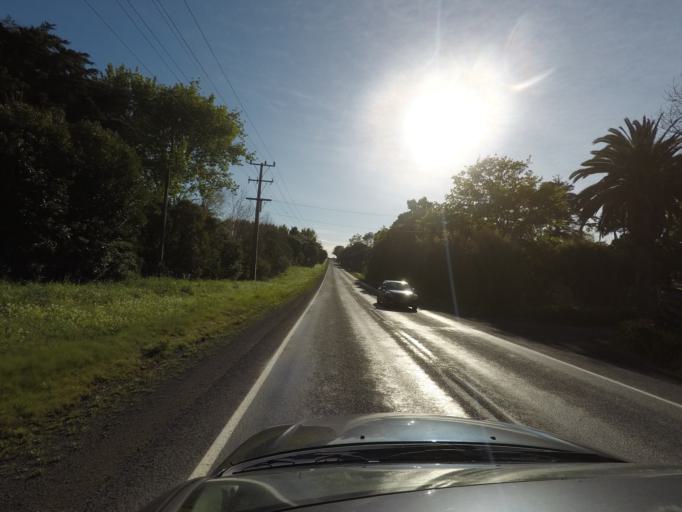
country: NZ
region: Auckland
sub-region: Auckland
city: Papakura
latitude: -37.0153
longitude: 174.9428
